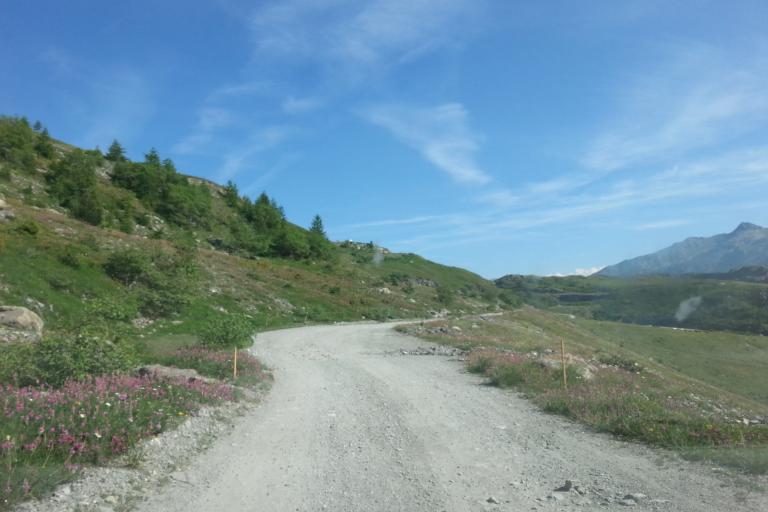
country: IT
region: Piedmont
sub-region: Provincia di Torino
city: Moncenisio
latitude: 45.2210
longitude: 6.9651
